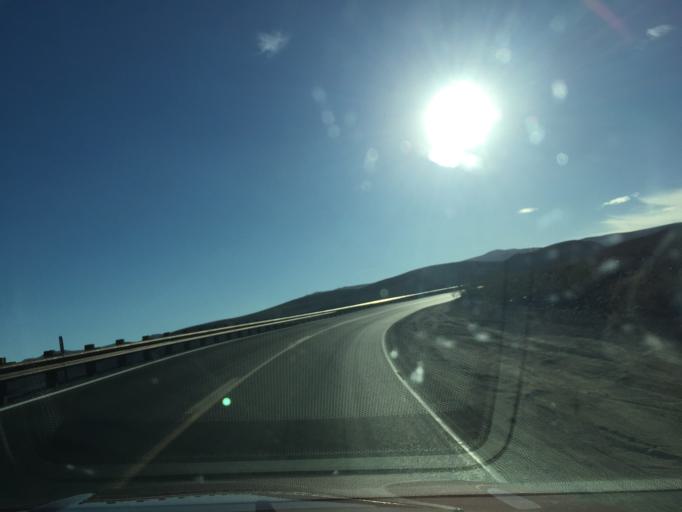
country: US
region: California
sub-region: San Bernardino County
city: Searles Valley
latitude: 36.3405
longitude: -117.5101
